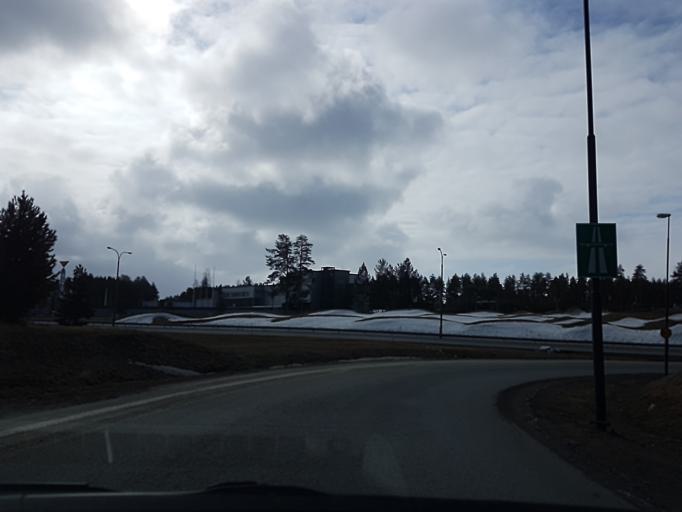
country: FI
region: North Karelia
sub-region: Joensuu
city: Joensuu
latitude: 62.6169
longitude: 29.7359
